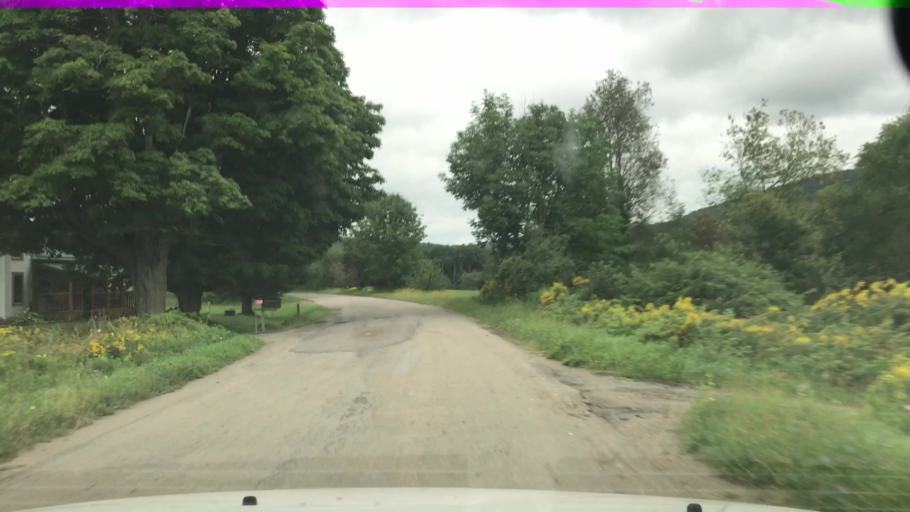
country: US
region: New York
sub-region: Cattaraugus County
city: Little Valley
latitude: 42.3156
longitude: -78.7219
